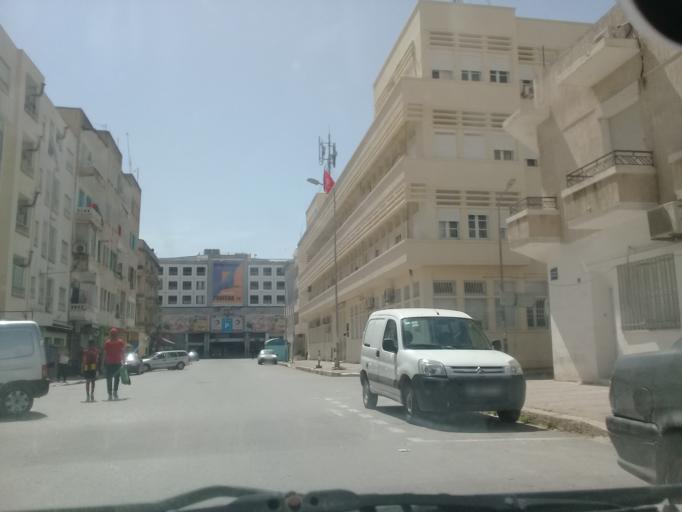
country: TN
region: Tunis
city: Tunis
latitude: 36.8127
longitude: 10.1829
